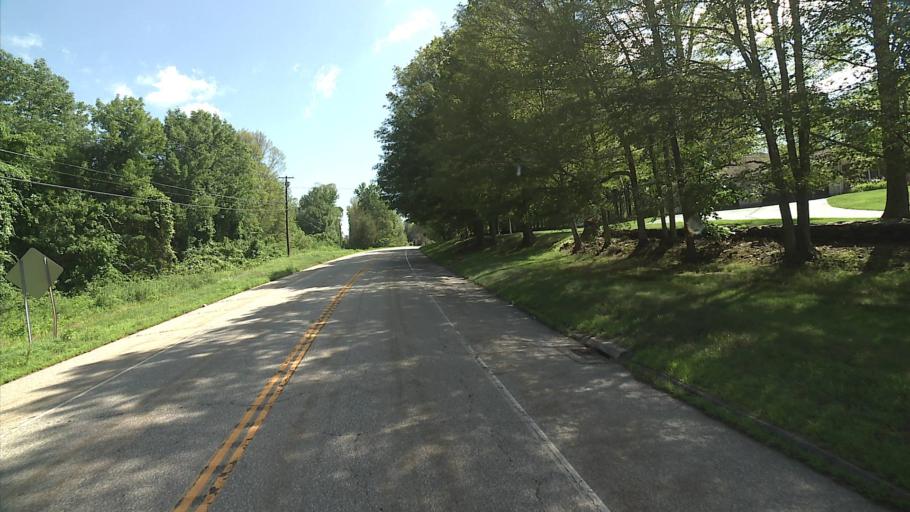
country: US
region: Connecticut
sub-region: Windham County
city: Plainfield Village
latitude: 41.7042
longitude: -71.9560
